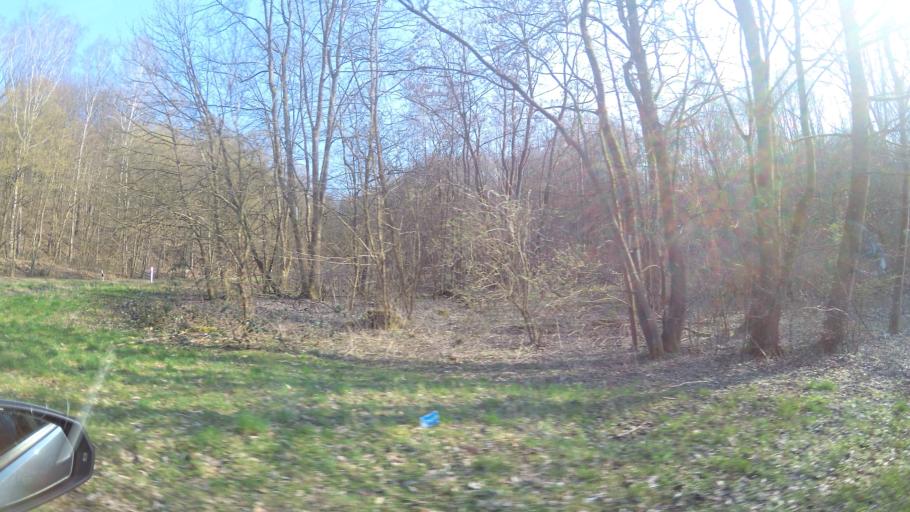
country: DE
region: Saarland
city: Sulzbach
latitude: 49.3042
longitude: 7.0778
